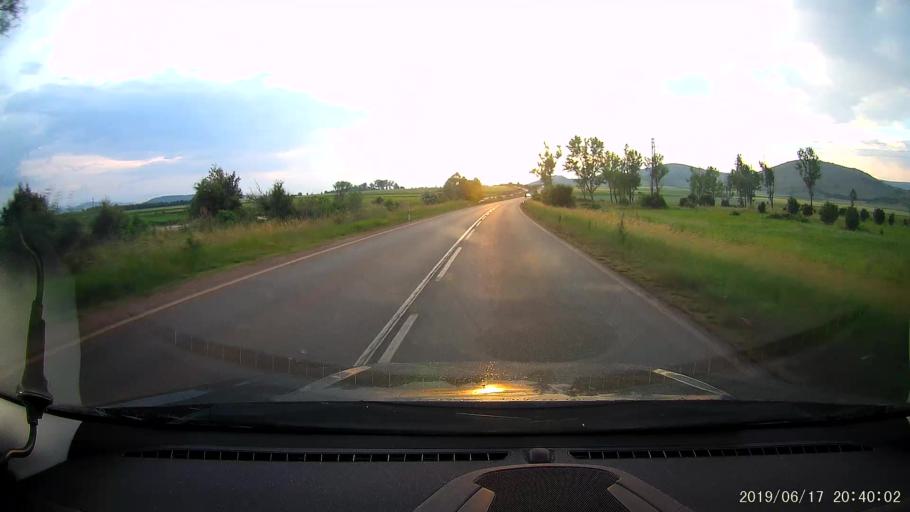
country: BG
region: Sofiya
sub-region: Obshtina Slivnitsa
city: Slivnitsa
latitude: 42.8832
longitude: 22.9937
